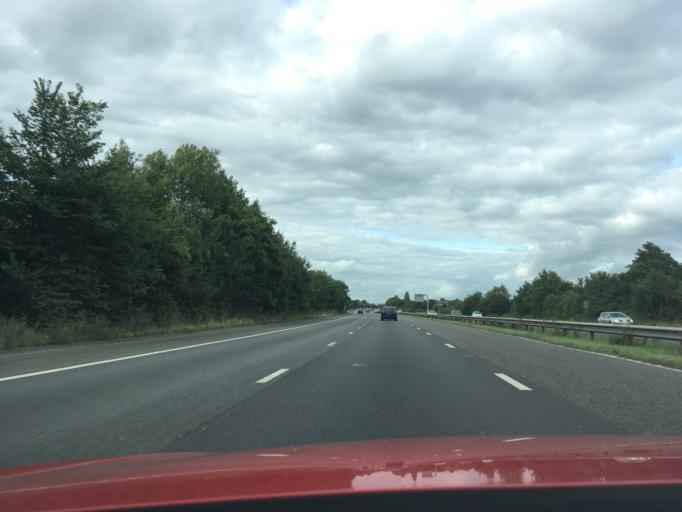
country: GB
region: England
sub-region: Gloucestershire
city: Stonehouse
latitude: 51.7695
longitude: -2.3127
